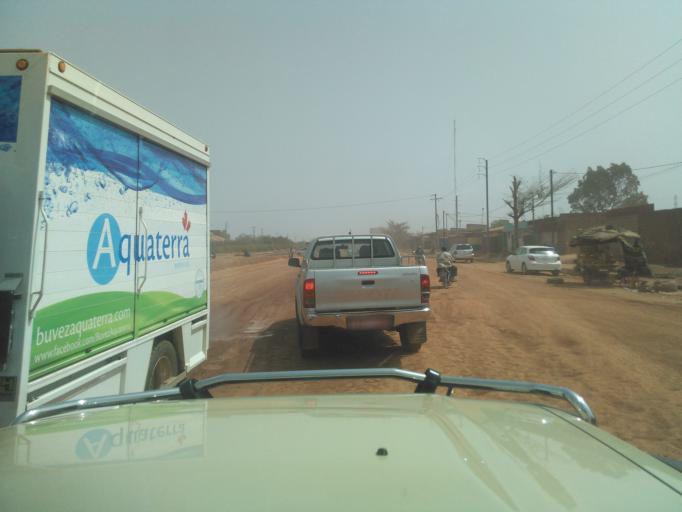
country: BF
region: Centre
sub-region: Kadiogo Province
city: Ouagadougou
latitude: 12.3898
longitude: -1.4818
